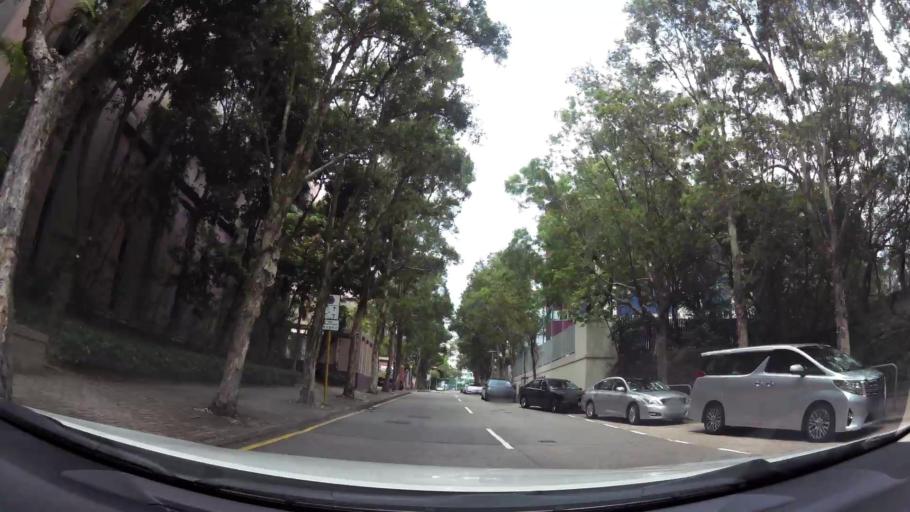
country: HK
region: Wanchai
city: Wan Chai
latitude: 22.2837
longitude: 114.1981
